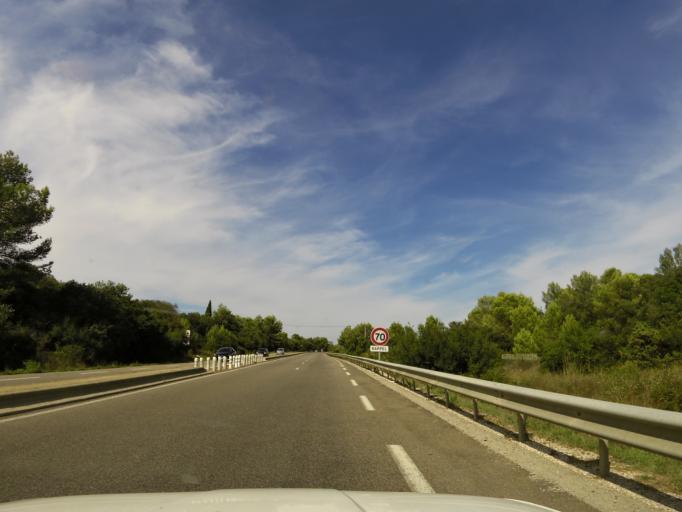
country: FR
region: Languedoc-Roussillon
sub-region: Departement du Gard
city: Nimes
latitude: 43.8497
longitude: 4.3184
